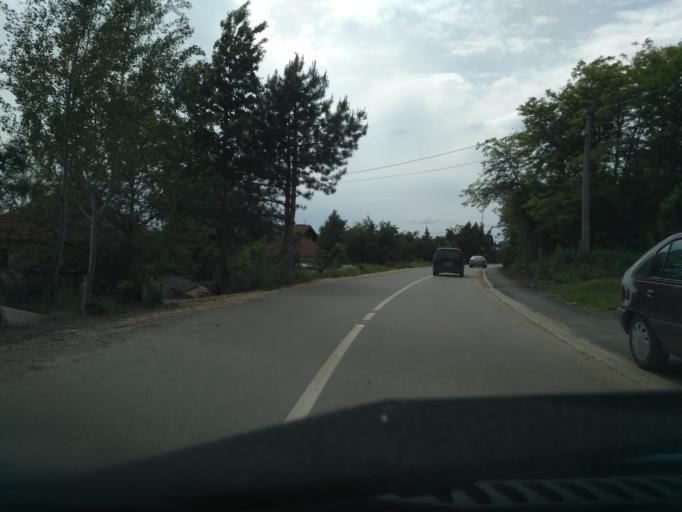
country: RS
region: Central Serbia
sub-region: Podunavski Okrug
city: Smederevska Palanka
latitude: 44.3571
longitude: 20.9767
